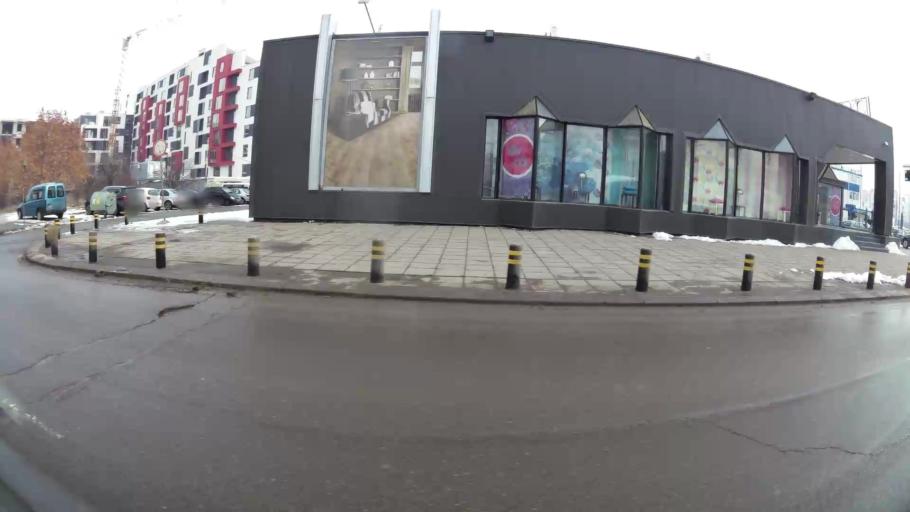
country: BG
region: Sofia-Capital
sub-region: Stolichna Obshtina
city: Sofia
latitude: 42.7120
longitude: 23.3799
